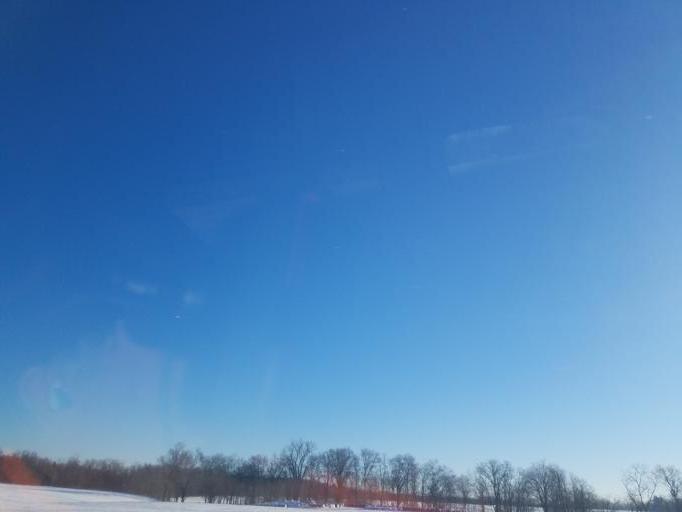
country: US
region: Ohio
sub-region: Delaware County
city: Sunbury
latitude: 40.2304
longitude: -82.9118
